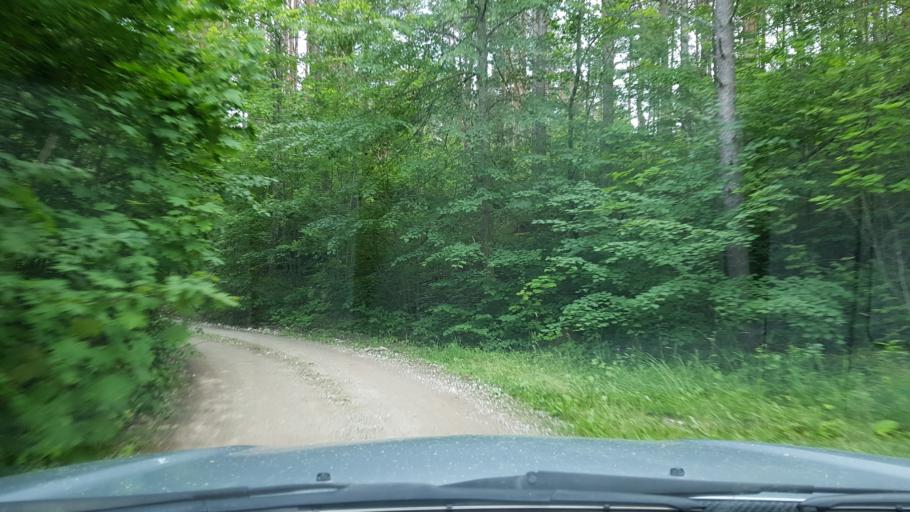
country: EE
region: Ida-Virumaa
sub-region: Narva-Joesuu linn
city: Narva-Joesuu
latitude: 59.4543
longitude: 28.0759
